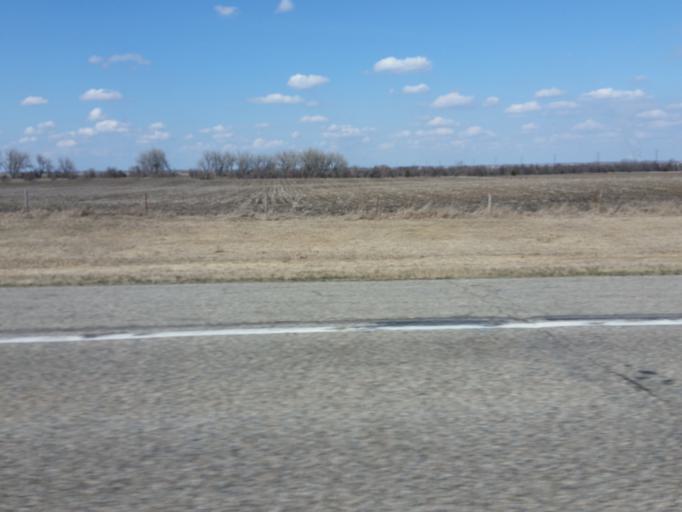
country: US
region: South Dakota
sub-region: Deuel County
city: Clear Lake
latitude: 44.9334
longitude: -96.5181
